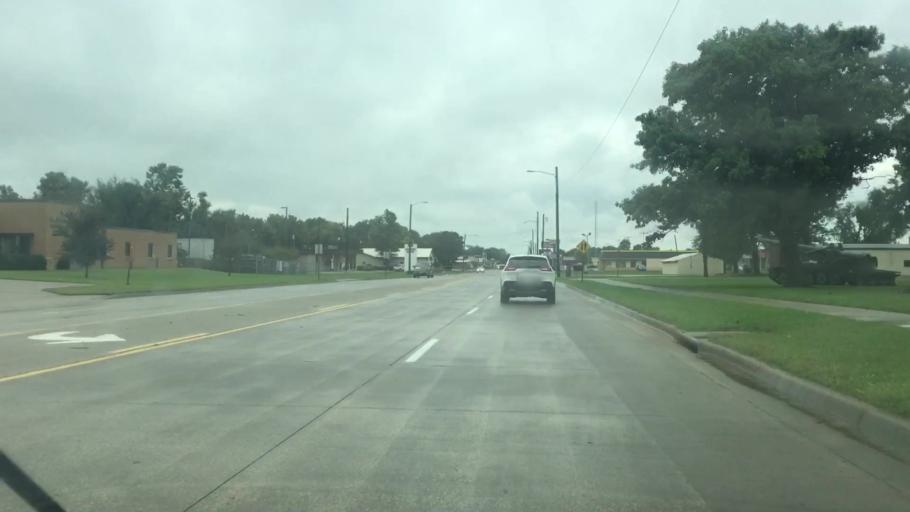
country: US
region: Kansas
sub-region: Allen County
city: Iola
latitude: 37.9326
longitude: -95.4091
